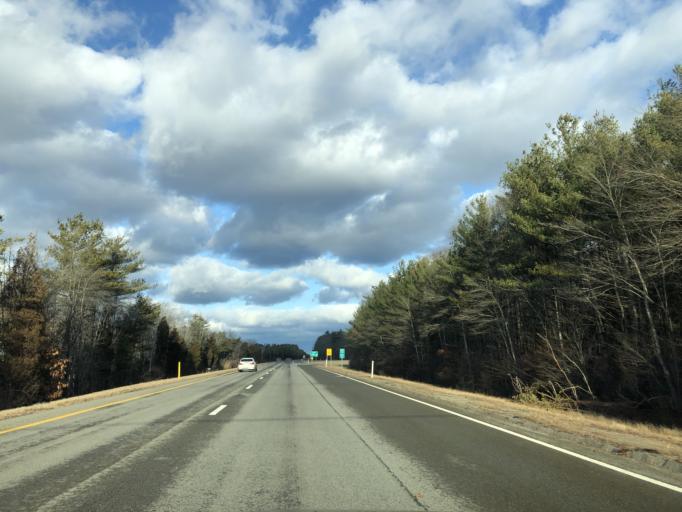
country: US
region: Massachusetts
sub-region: Plymouth County
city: Mattapoisett Center
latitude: 41.6750
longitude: -70.8219
